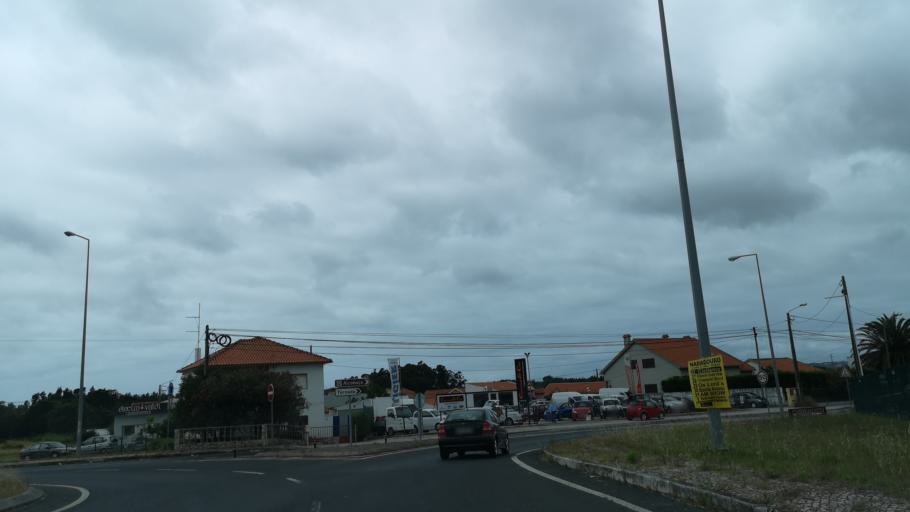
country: PT
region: Leiria
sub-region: Caldas da Rainha
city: Caldas da Rainha
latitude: 39.4403
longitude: -9.1295
